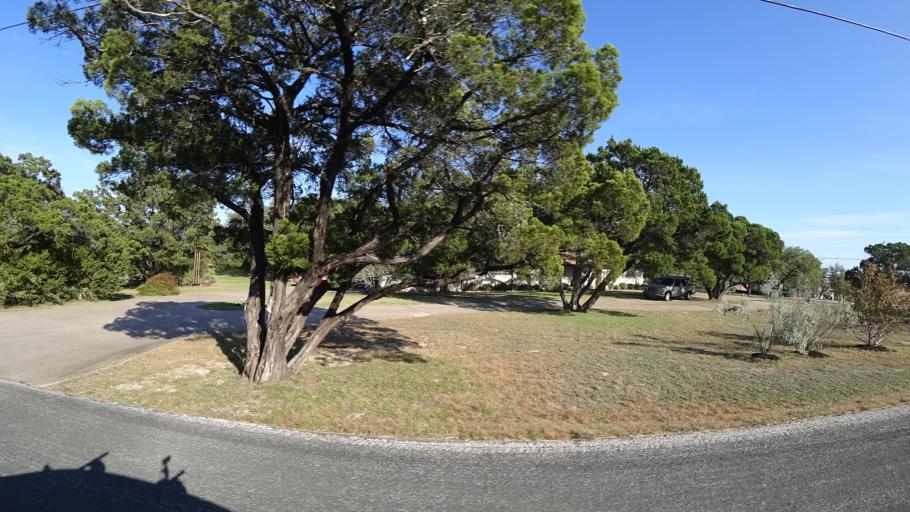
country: US
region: Texas
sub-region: Travis County
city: Bee Cave
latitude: 30.2333
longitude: -97.9286
